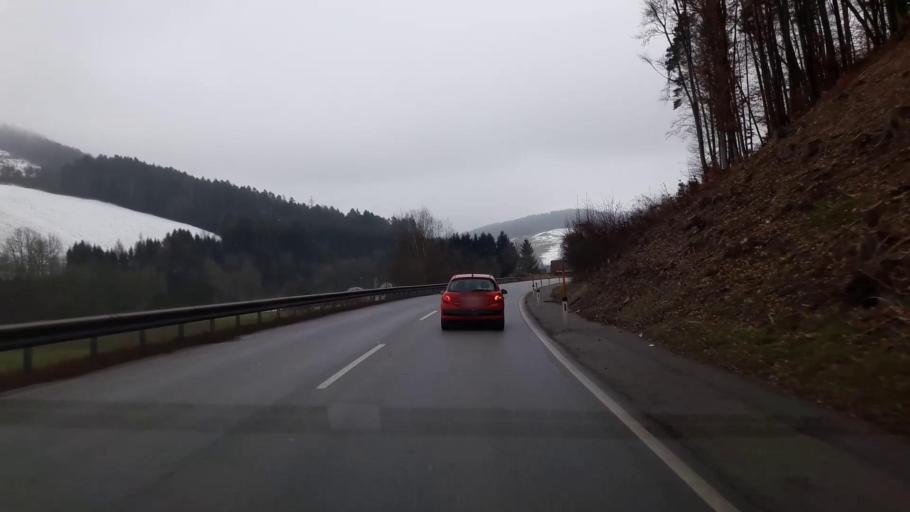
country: AT
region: Lower Austria
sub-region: Politischer Bezirk Neunkirchen
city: Edlitz
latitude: 47.5959
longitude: 16.1133
